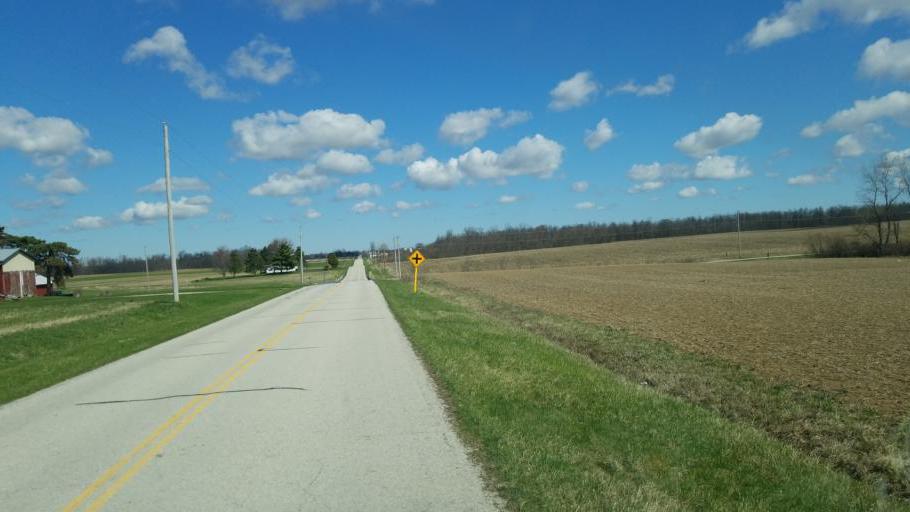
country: US
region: Ohio
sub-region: Sandusky County
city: Mount Carmel
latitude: 41.1453
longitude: -82.9382
